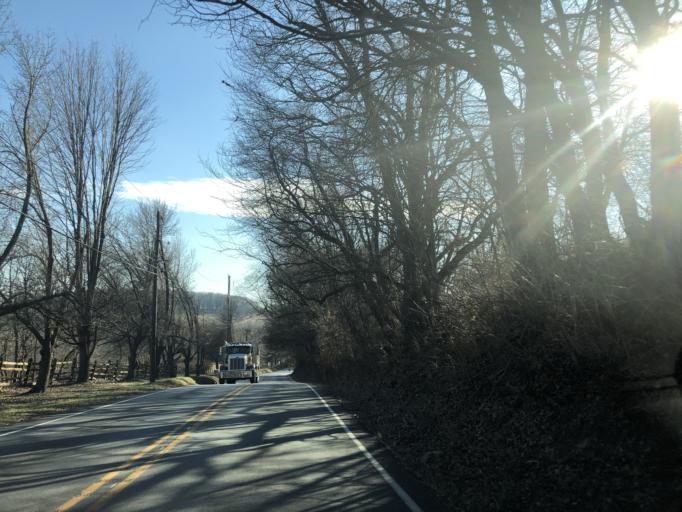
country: US
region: Pennsylvania
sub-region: Chester County
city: South Coatesville
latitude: 39.9360
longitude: -75.8310
